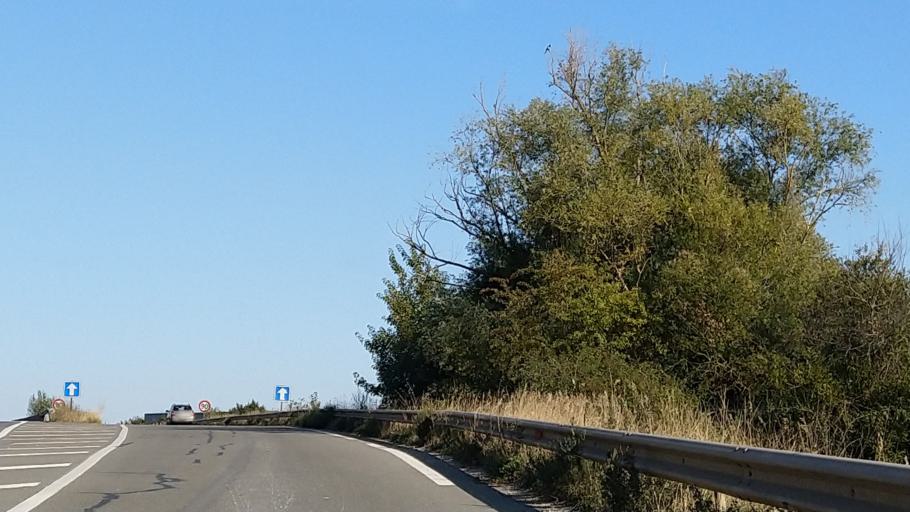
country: FR
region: Ile-de-France
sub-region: Departement de Seine-et-Marne
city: Mitry-Mory
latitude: 48.9905
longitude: 2.6570
